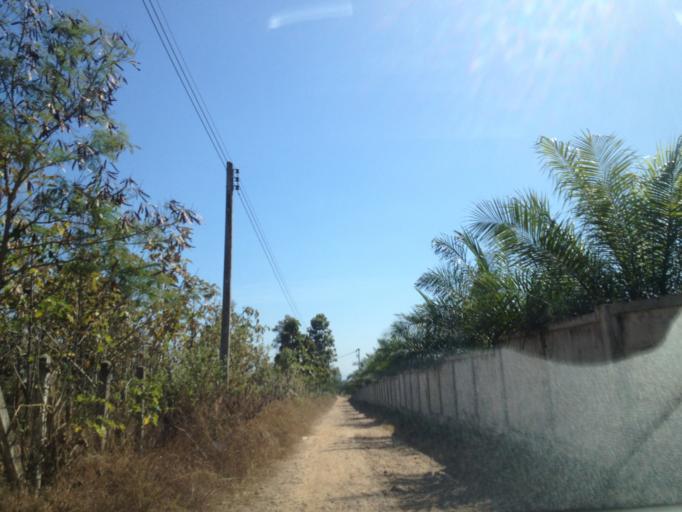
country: TH
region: Chiang Mai
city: San Pa Tong
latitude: 18.6720
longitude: 98.8691
